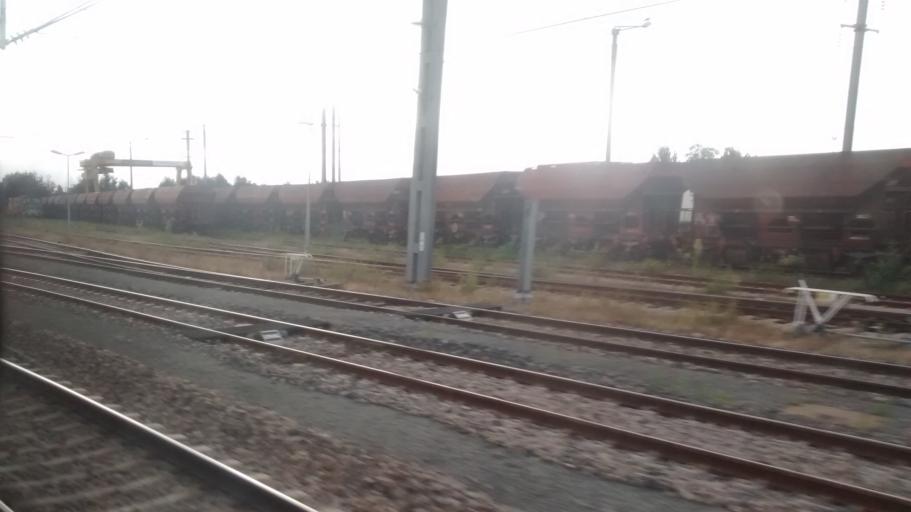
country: FR
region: Brittany
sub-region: Departement d'Ille-et-Vilaine
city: Chantepie
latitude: 48.1085
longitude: -1.6302
